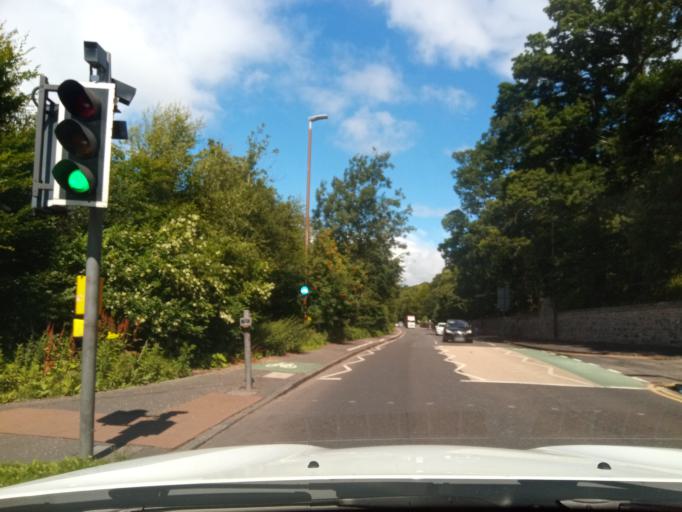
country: GB
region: Scotland
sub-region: Stirling
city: Bridge of Allan
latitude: 56.1412
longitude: -3.9264
